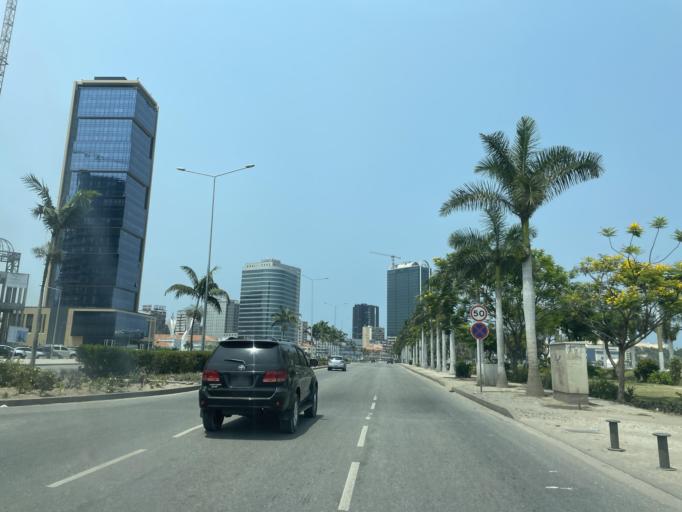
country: AO
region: Luanda
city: Luanda
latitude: -8.8101
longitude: 13.2330
